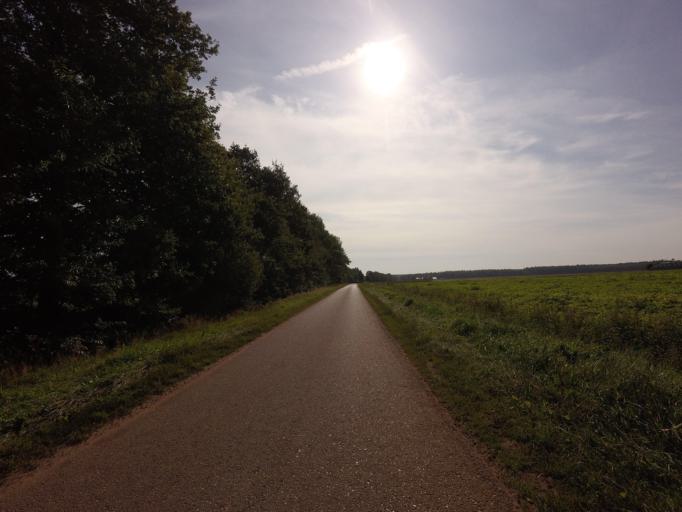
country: NL
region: Drenthe
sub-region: Gemeente Borger-Odoorn
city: Borger
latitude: 52.9336
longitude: 6.6992
